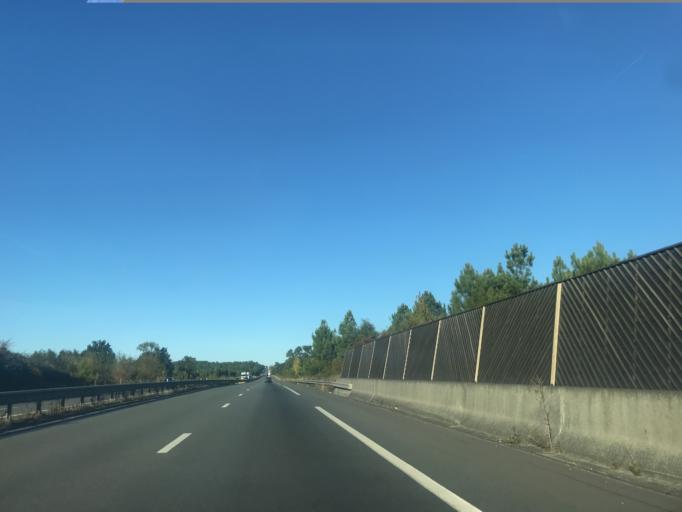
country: FR
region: Poitou-Charentes
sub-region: Departement de la Charente-Maritime
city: Montlieu-la-Garde
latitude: 45.2073
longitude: -0.2985
